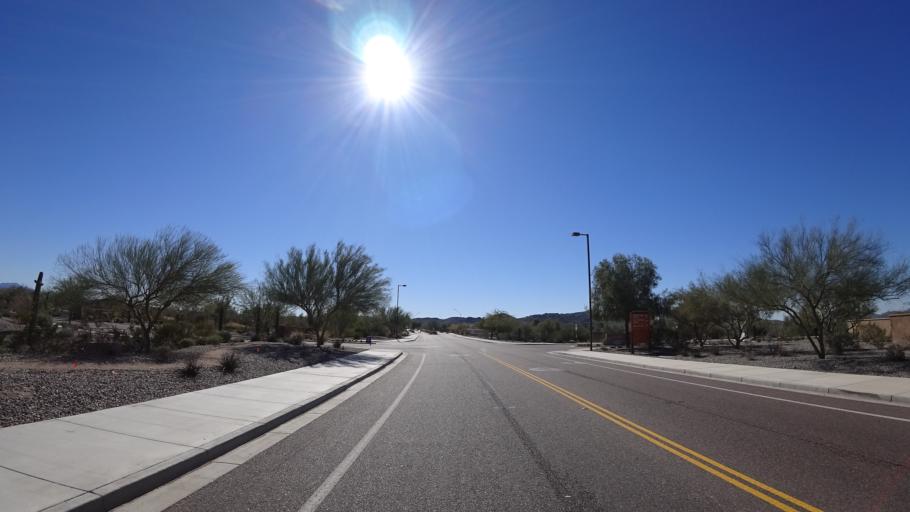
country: US
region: Arizona
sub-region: Maricopa County
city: Goodyear
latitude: 33.3354
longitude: -112.4480
